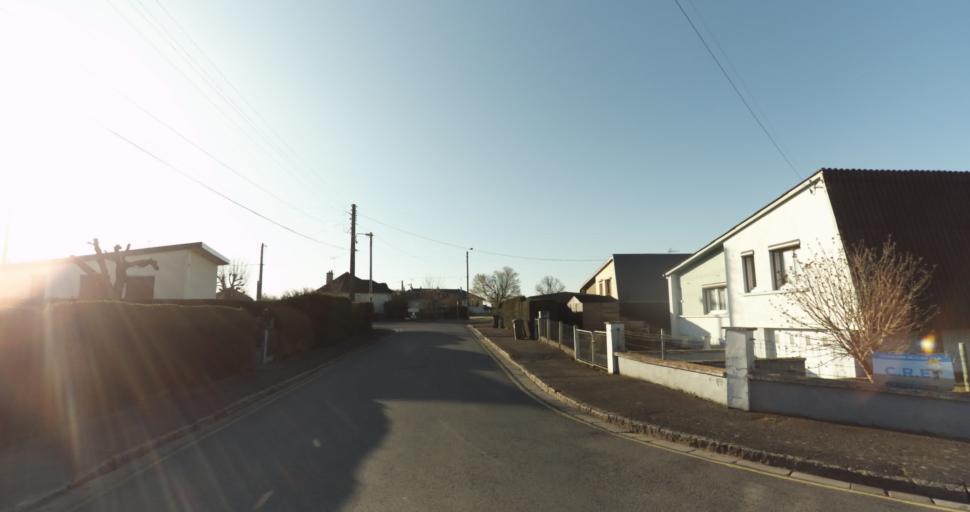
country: FR
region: Lower Normandy
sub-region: Departement du Calvados
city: Saint-Pierre-sur-Dives
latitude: 49.0124
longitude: -0.0320
